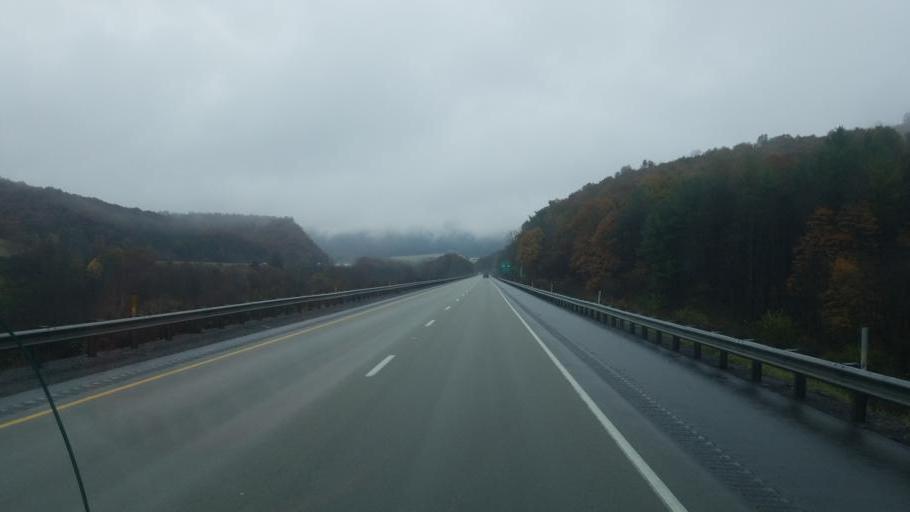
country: US
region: Pennsylvania
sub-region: Centre County
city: Milesburg
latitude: 40.9636
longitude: -77.7861
